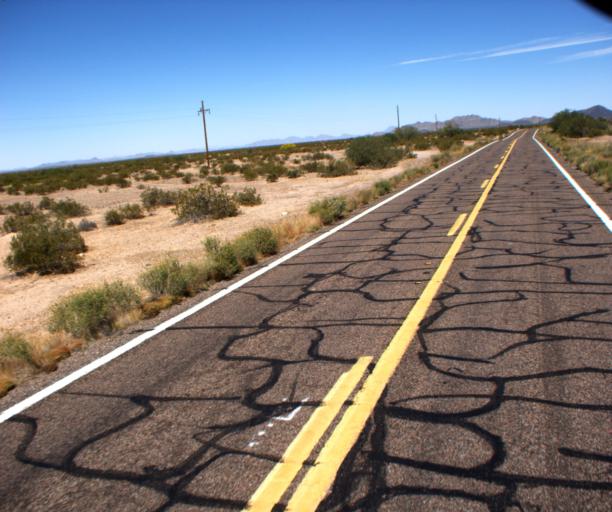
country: US
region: Arizona
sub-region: Maricopa County
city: Gila Bend
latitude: 32.6825
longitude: -112.8556
